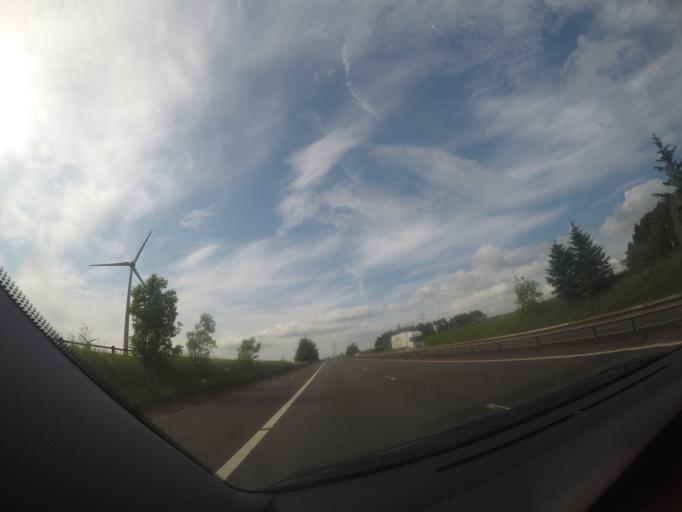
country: GB
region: Scotland
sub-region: South Lanarkshire
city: Douglas
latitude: 55.6032
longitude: -3.8389
